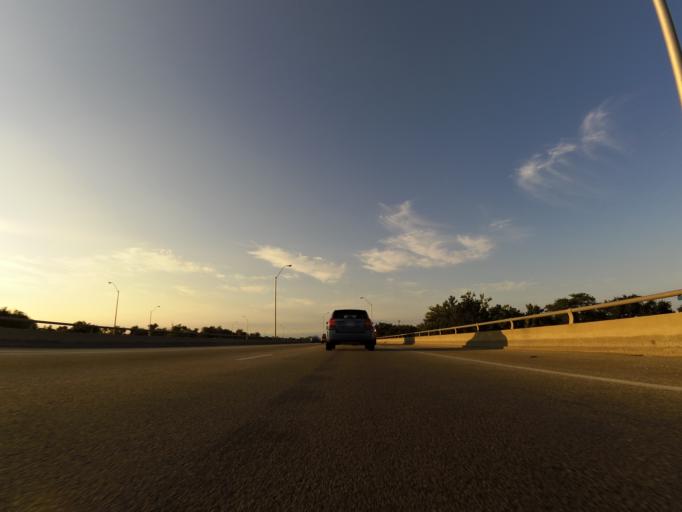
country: US
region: Kansas
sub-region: Sedgwick County
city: Wichita
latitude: 37.7131
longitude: -97.3220
